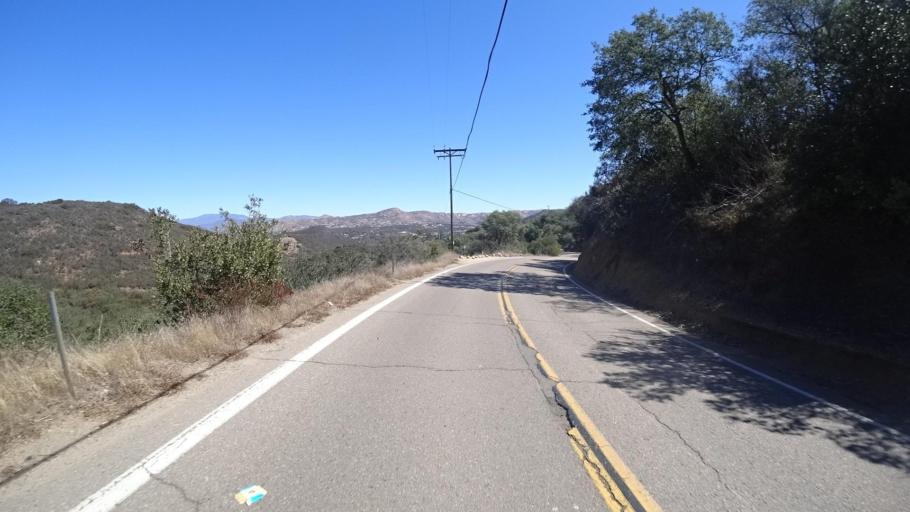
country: US
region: California
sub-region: San Diego County
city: Harbison Canyon
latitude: 32.7474
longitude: -116.7963
